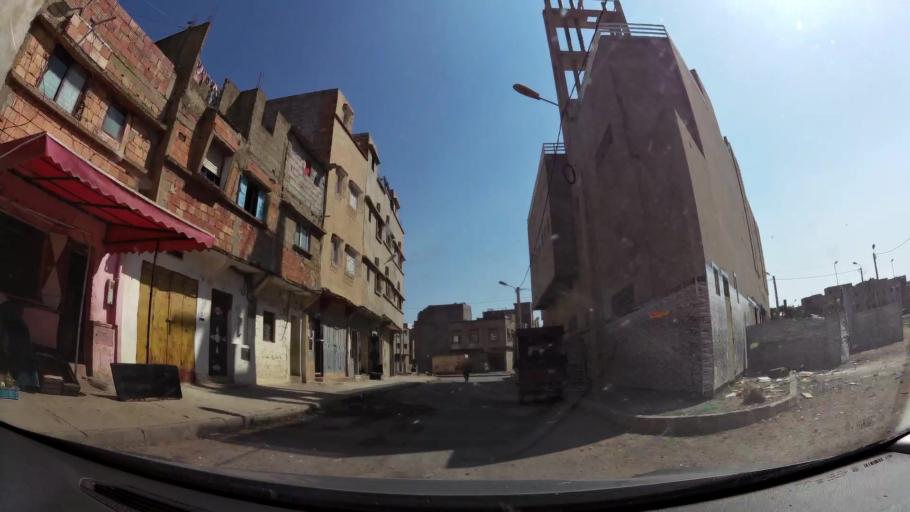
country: MA
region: Rabat-Sale-Zemmour-Zaer
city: Sale
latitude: 34.0708
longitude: -6.7710
